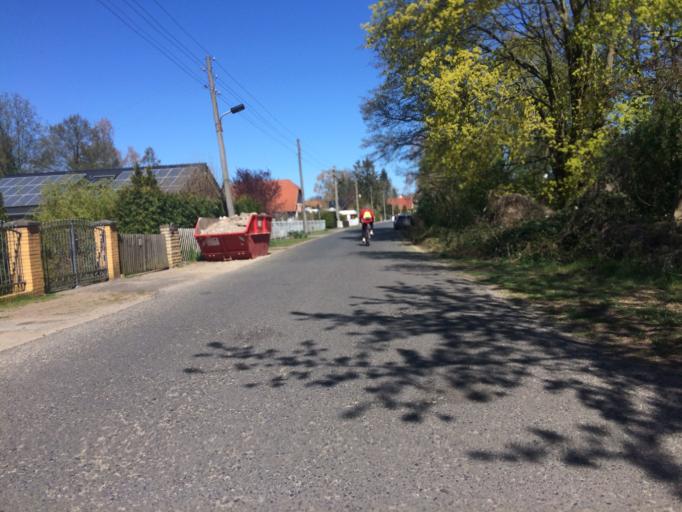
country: DE
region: Berlin
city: Rahnsdorf
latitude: 52.4293
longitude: 13.7128
